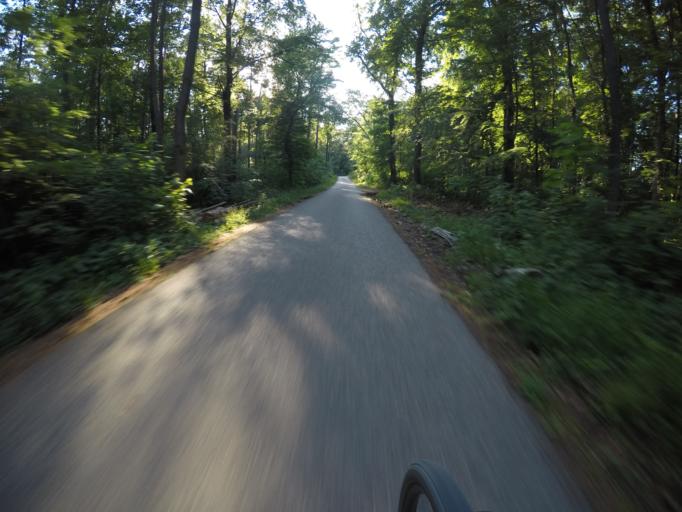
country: DE
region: Baden-Wuerttemberg
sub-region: Regierungsbezirk Stuttgart
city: Fellbach
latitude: 48.7846
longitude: 9.3039
